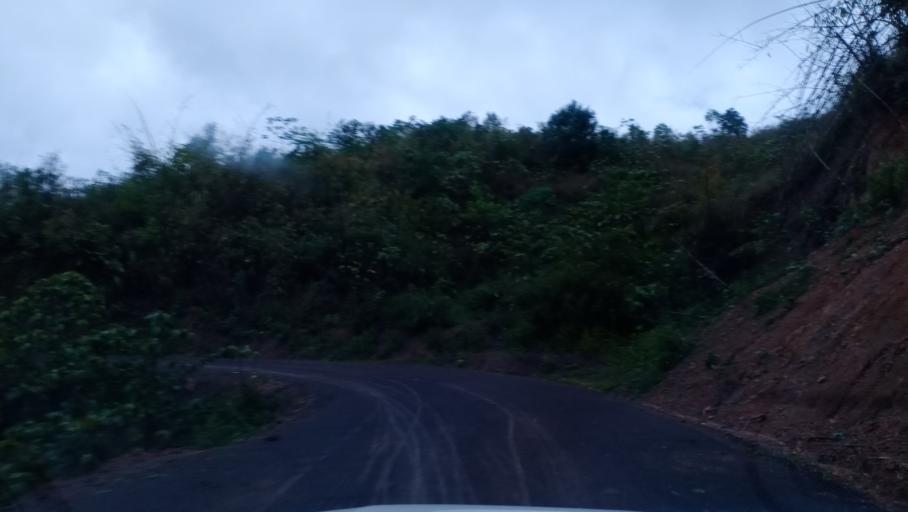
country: VN
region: Huyen Dien Bien
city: Dien Bien Phu
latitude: 21.3309
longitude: 102.7175
